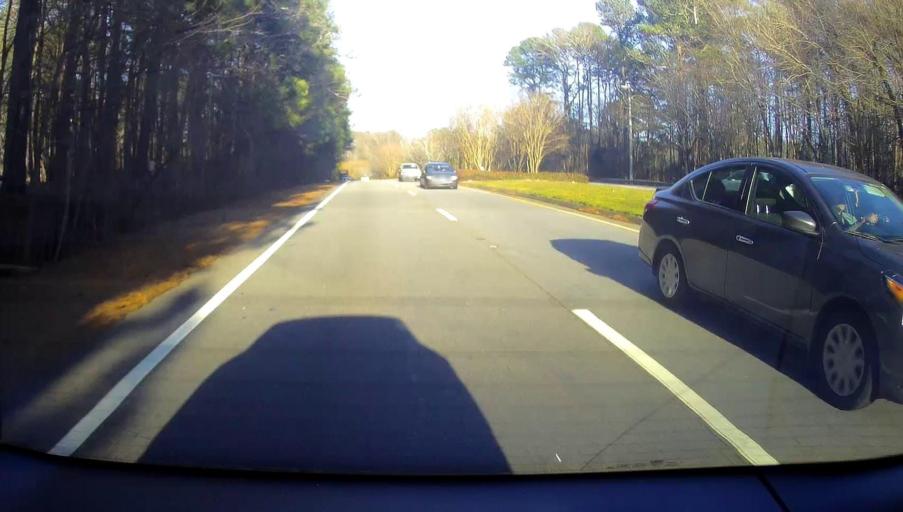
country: US
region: Georgia
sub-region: Fayette County
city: Peachtree City
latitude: 33.4035
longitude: -84.5747
